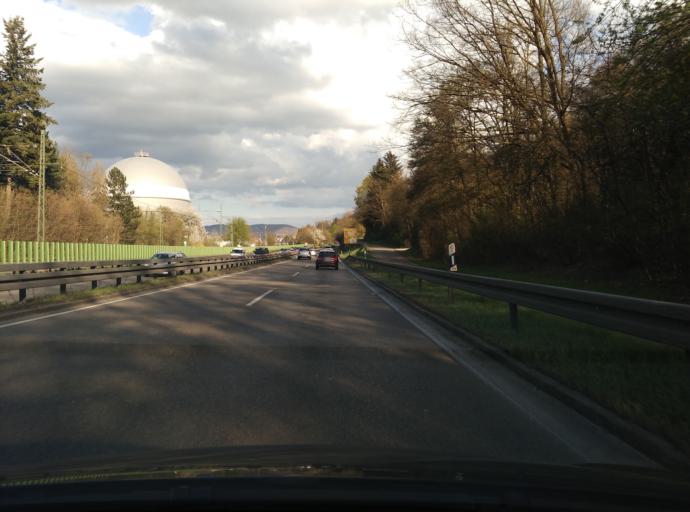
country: DE
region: Baden-Wuerttemberg
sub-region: Tuebingen Region
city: Reutlingen
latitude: 48.4929
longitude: 9.1841
